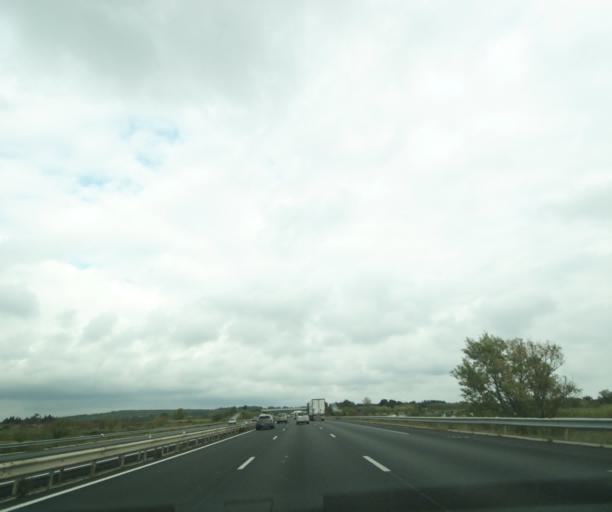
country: FR
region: Languedoc-Roussillon
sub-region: Departement de l'Herault
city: Loupian
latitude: 43.4551
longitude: 3.6070
